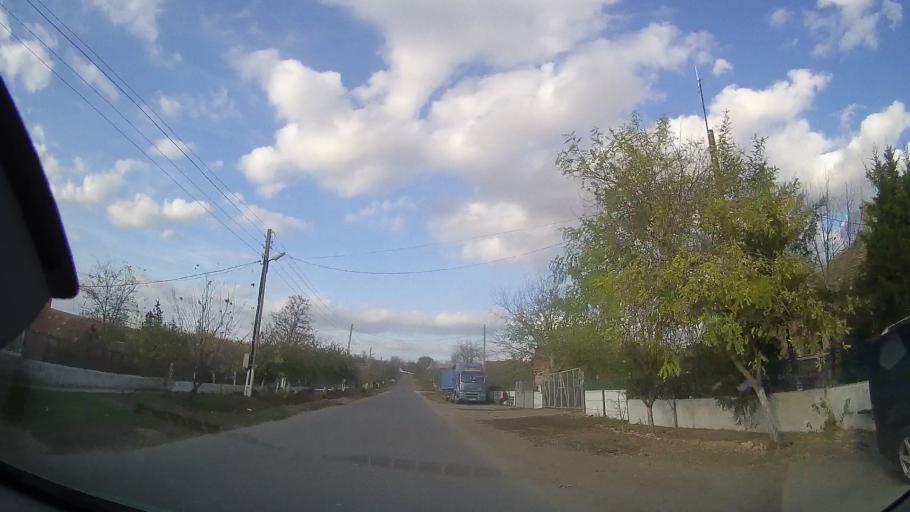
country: RO
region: Constanta
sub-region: Comuna Cerchezu
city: Cerchezu
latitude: 43.8578
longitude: 28.1013
